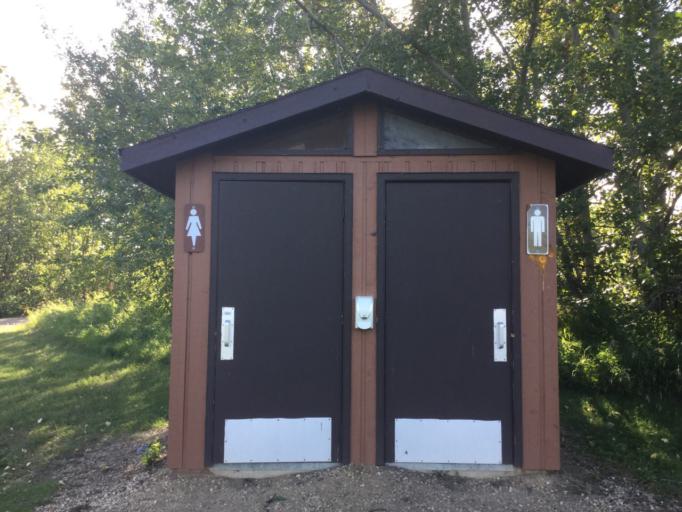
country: CA
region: Alberta
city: Sylvan Lake
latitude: 52.4703
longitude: -113.9836
